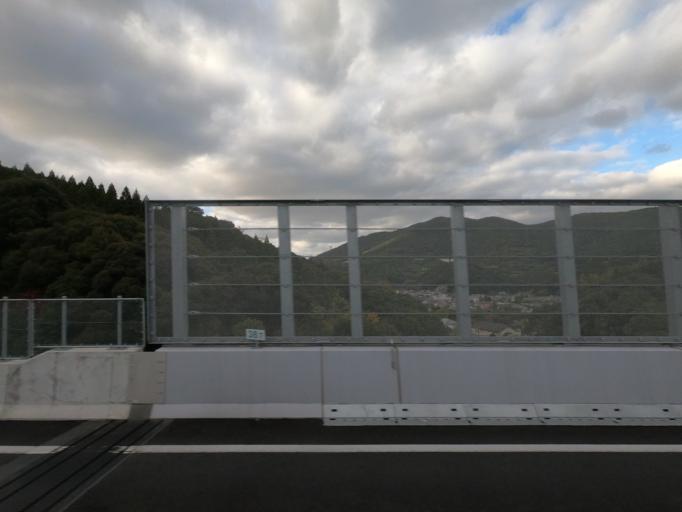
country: JP
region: Kumamoto
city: Minamata
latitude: 32.2300
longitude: 130.4491
